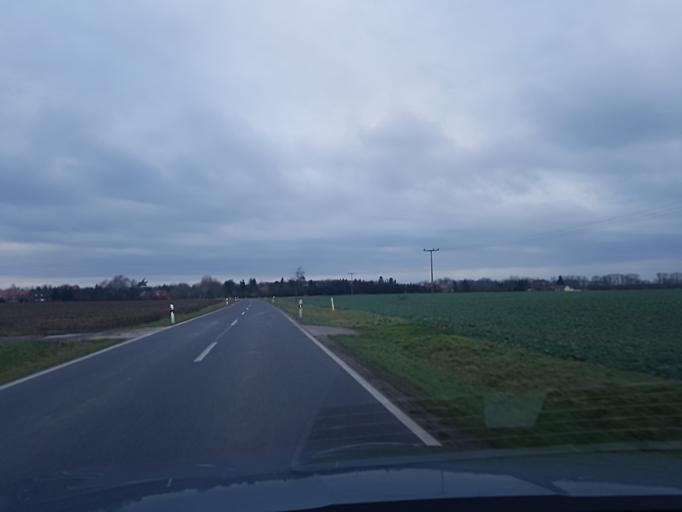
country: DE
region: Brandenburg
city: Sonnewalde
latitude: 51.6948
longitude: 13.6596
